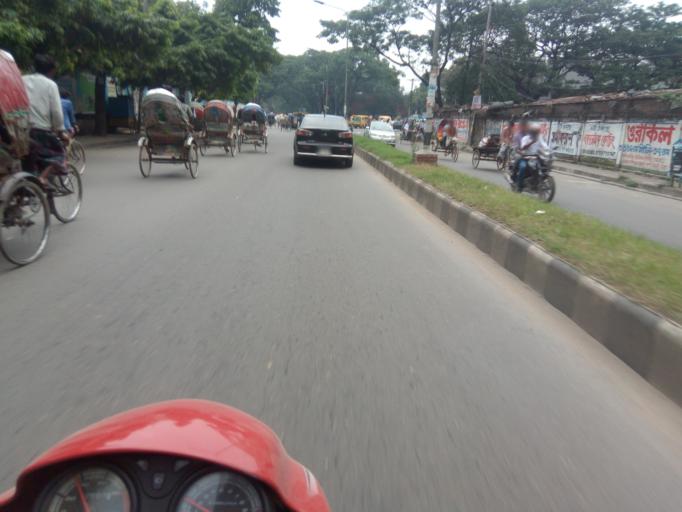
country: BD
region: Dhaka
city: Azimpur
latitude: 23.7274
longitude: 90.3886
